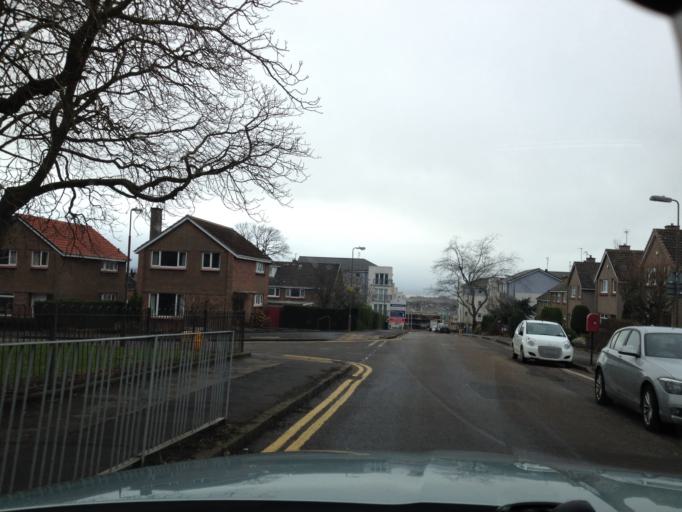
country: GB
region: Scotland
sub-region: Edinburgh
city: Colinton
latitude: 55.9515
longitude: -3.2805
